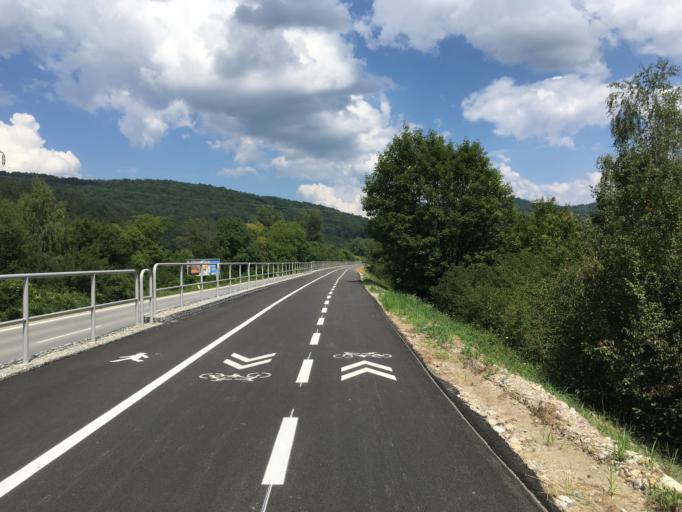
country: SK
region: Nitriansky
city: Puchov
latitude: 49.1347
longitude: 18.3370
